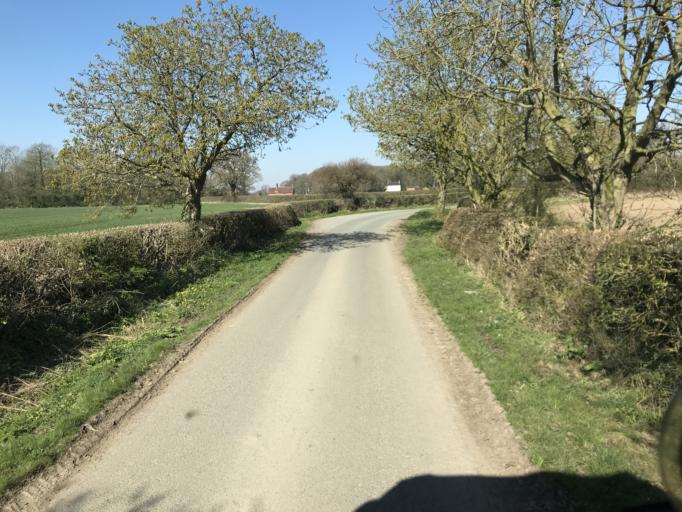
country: GB
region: England
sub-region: Cheshire West and Chester
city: Aldford
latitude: 53.1277
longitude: -2.8580
